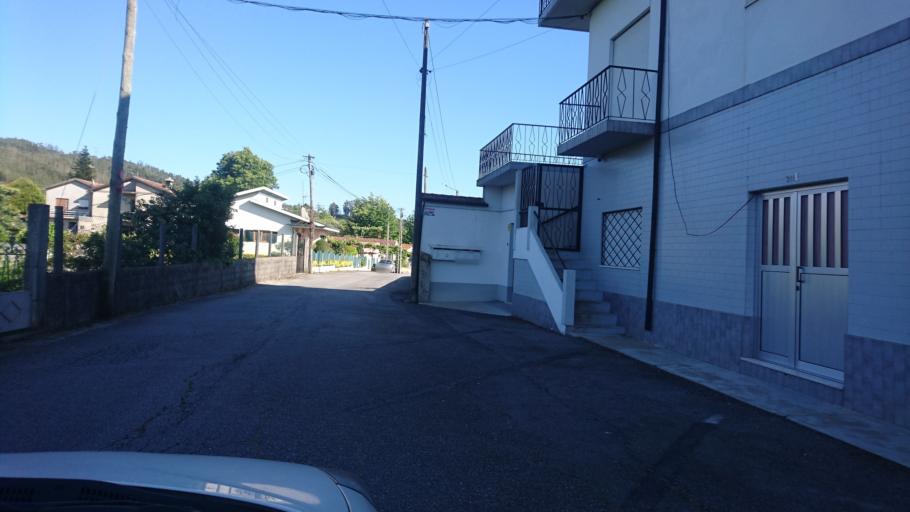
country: PT
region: Porto
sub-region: Paredes
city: Recarei
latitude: 41.1472
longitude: -8.3876
